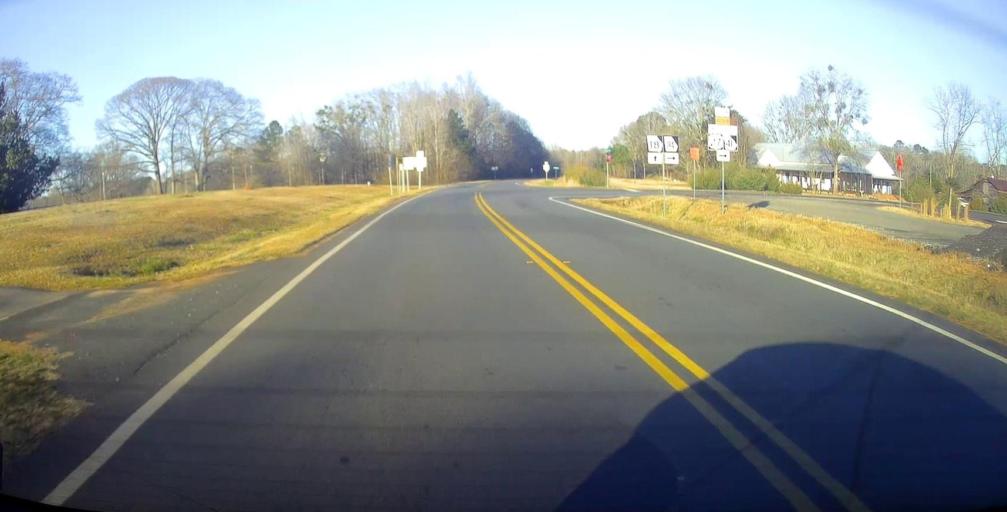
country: US
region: Georgia
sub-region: Harris County
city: Pine Mountain
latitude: 32.9217
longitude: -84.7689
